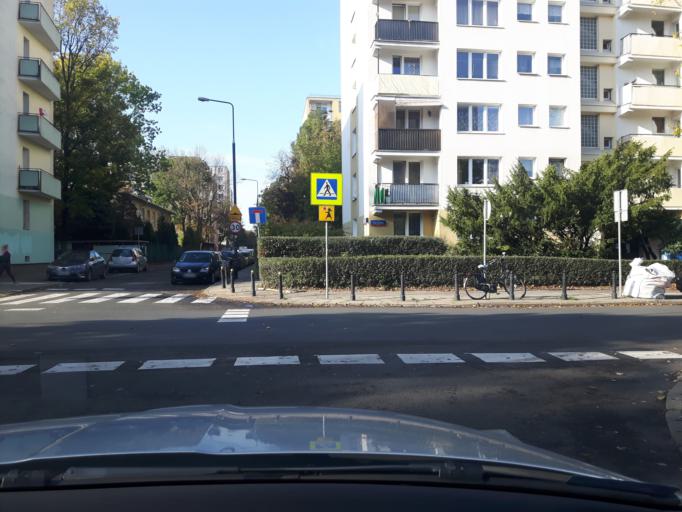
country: PL
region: Masovian Voivodeship
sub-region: Warszawa
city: Wola
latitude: 52.2516
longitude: 20.9890
